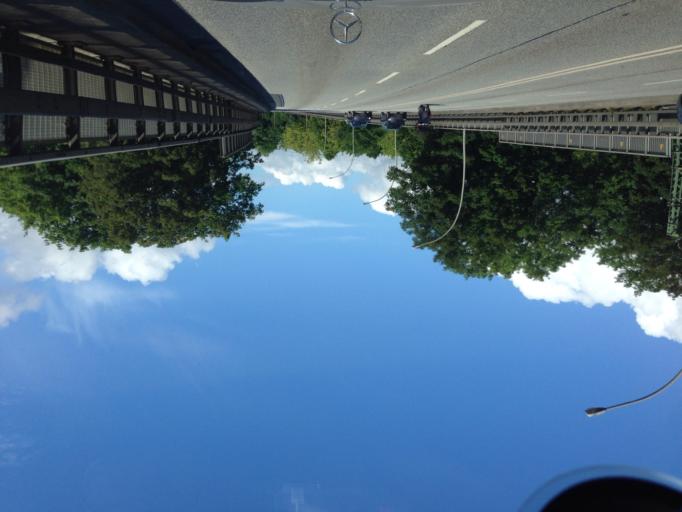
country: DE
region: Hamburg
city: Marienthal
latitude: 53.5686
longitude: 10.0733
